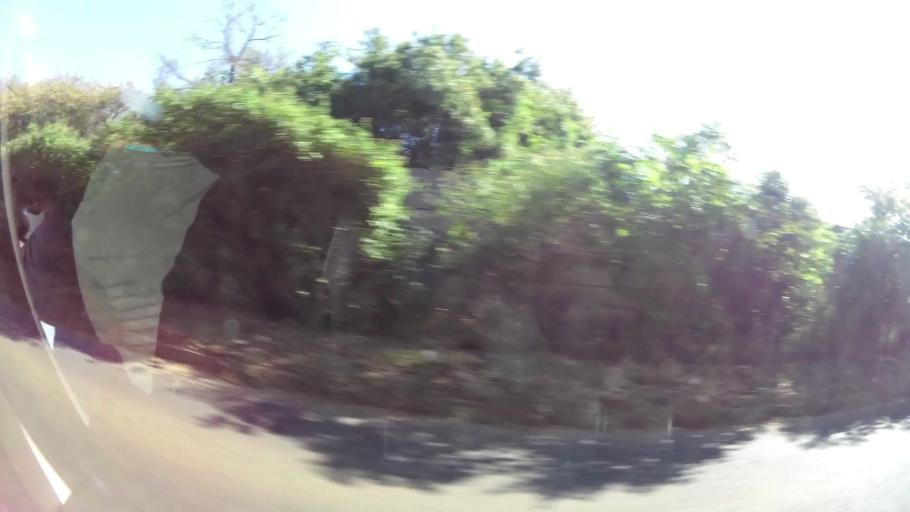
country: ZA
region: Gauteng
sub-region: City of Tshwane Metropolitan Municipality
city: Pretoria
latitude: -25.6723
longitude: 28.2547
